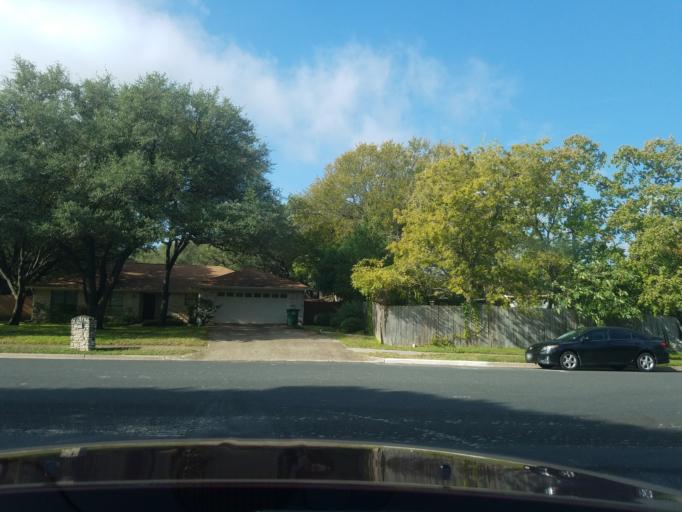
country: US
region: Texas
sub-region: Williamson County
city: Jollyville
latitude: 30.4501
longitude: -97.7774
